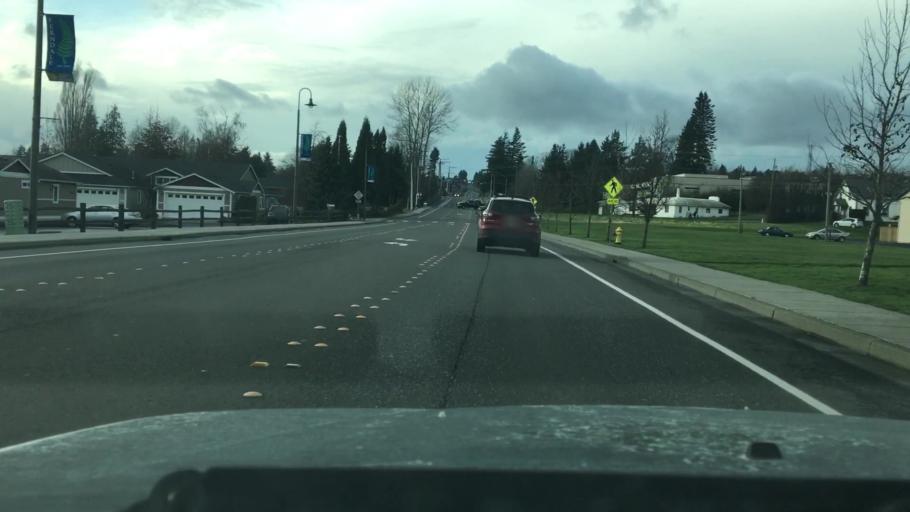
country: US
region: Washington
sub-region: Whatcom County
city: Ferndale
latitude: 48.8484
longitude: -122.5991
